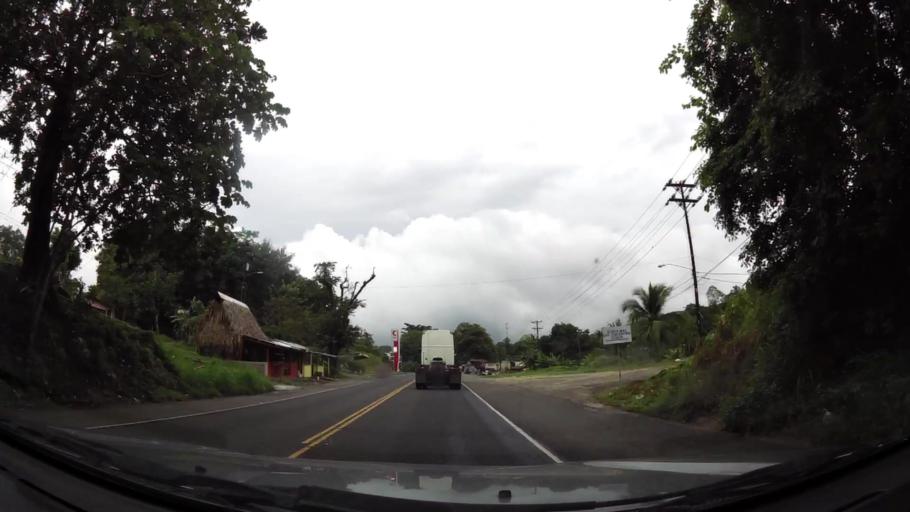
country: PA
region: Colon
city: Nuevo Vigia
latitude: 9.2288
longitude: -79.6286
